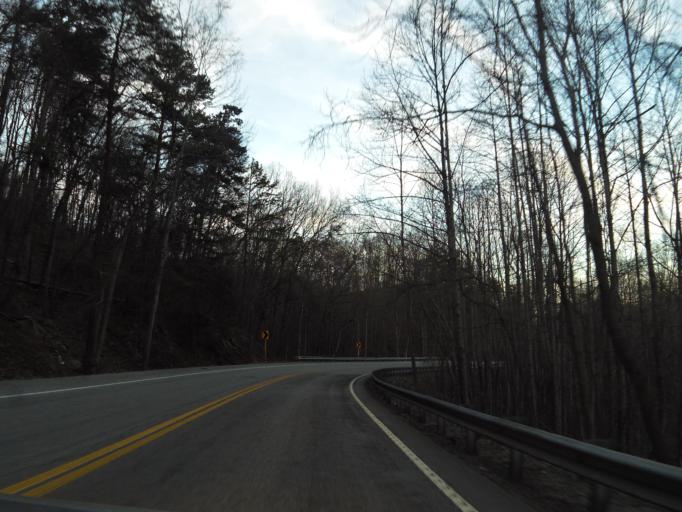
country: US
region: Tennessee
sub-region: Roane County
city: Rockwood
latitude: 35.8558
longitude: -84.7190
